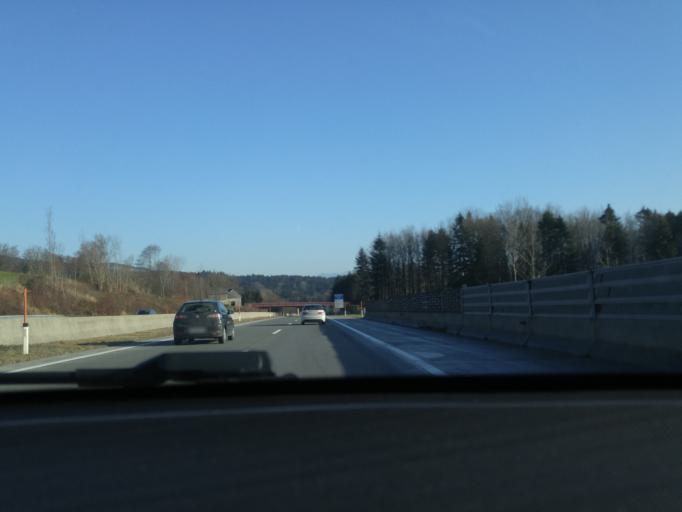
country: AT
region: Salzburg
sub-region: Politischer Bezirk Salzburg-Umgebung
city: Plainfeld
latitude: 47.8558
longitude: 13.2072
